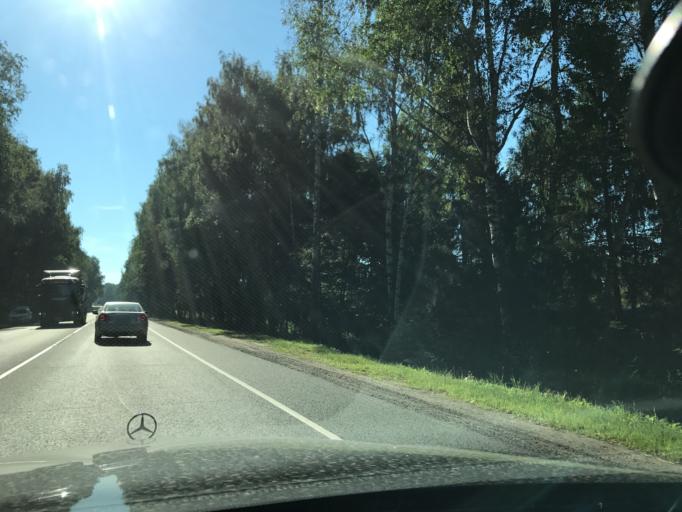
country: RU
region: Moskovskaya
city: Noginsk-9
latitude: 56.1012
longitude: 38.6559
